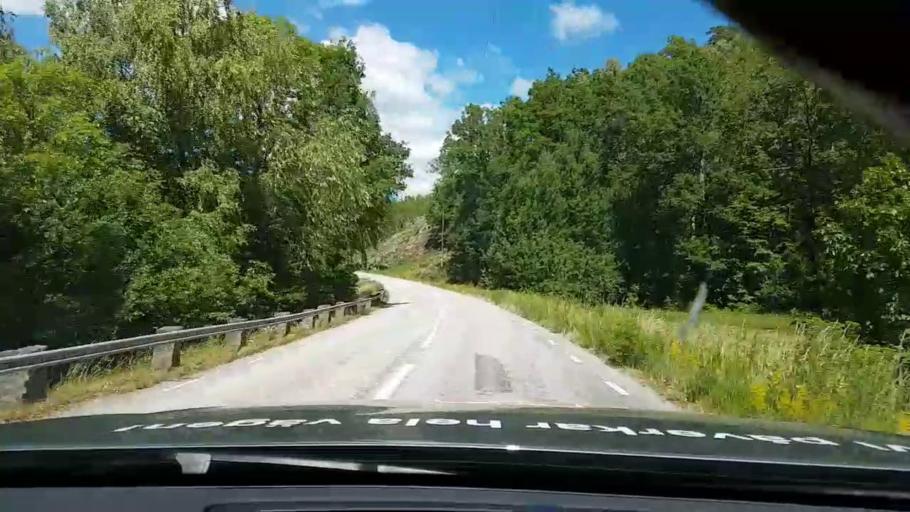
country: SE
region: Kalmar
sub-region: Vasterviks Kommun
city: Overum
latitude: 58.0564
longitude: 16.4064
